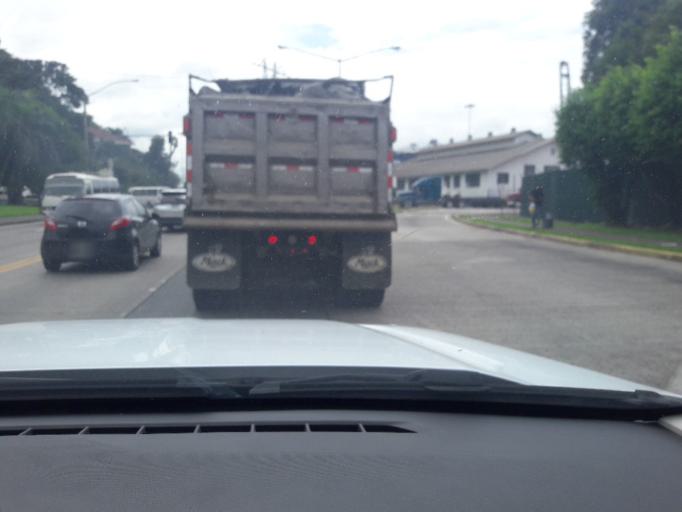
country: PA
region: Panama
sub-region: Distrito de Panama
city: Ancon
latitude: 8.9578
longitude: -79.5599
